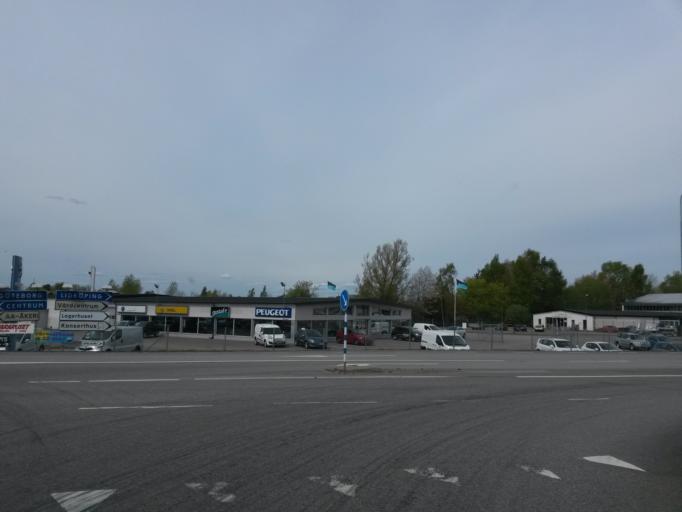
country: SE
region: Vaestra Goetaland
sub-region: Vara Kommun
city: Vara
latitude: 58.2569
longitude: 12.9711
